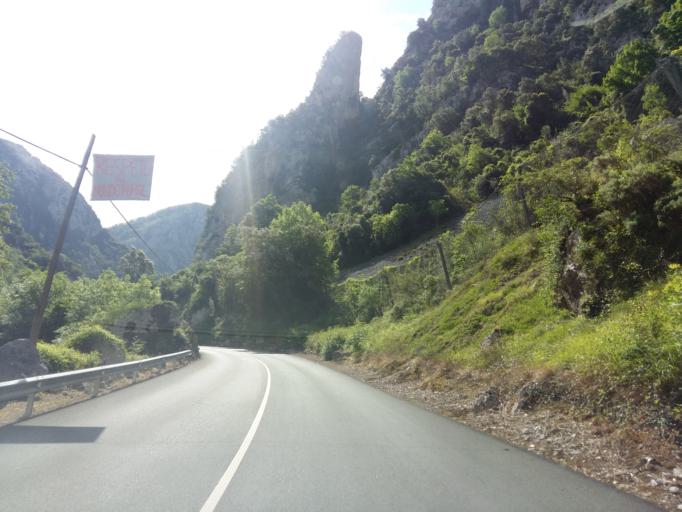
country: ES
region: Cantabria
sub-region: Provincia de Cantabria
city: Tresviso
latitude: 43.2494
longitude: -4.5996
